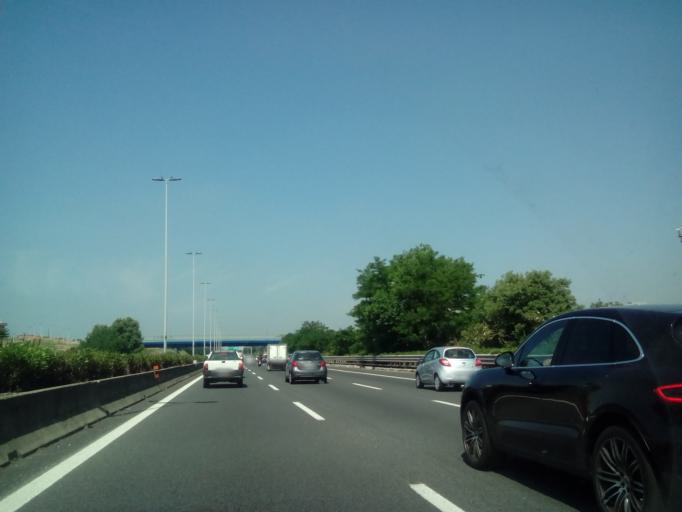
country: IT
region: Latium
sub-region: Citta metropolitana di Roma Capitale
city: Selcetta
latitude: 41.7960
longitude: 12.4940
